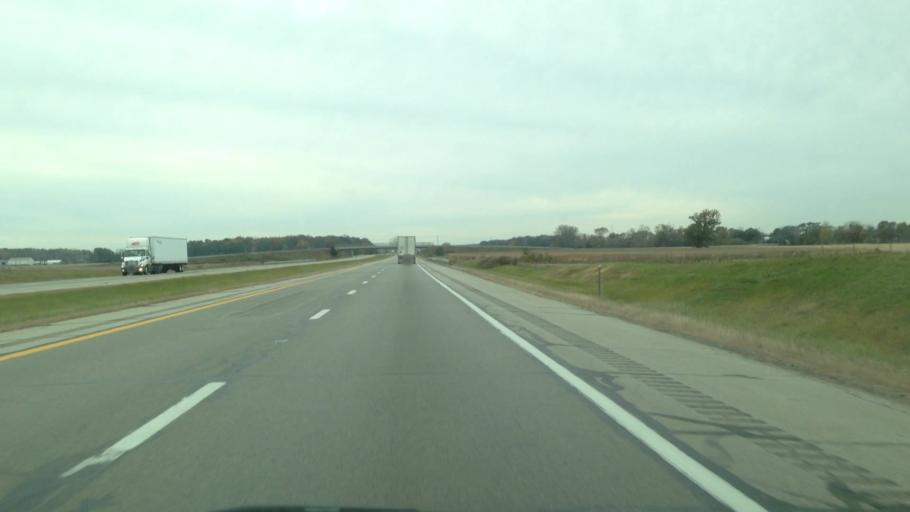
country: US
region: Ohio
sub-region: Williams County
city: Montpelier
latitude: 41.6170
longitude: -84.6255
